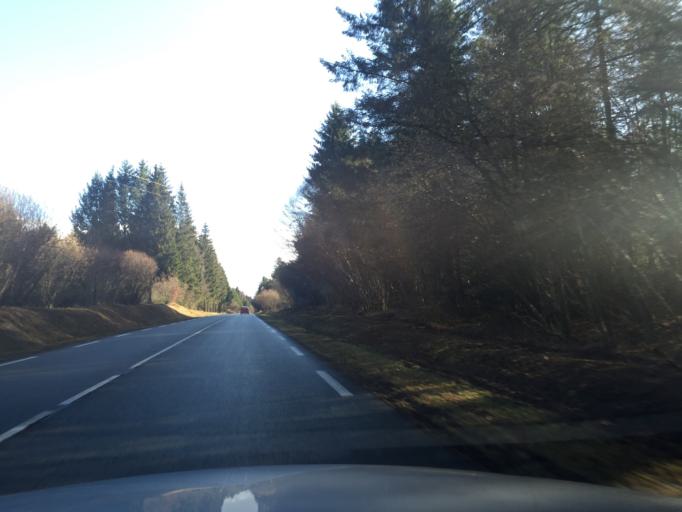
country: FR
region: Auvergne
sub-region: Departement du Puy-de-Dome
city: Orcines
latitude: 45.8110
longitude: 2.9620
